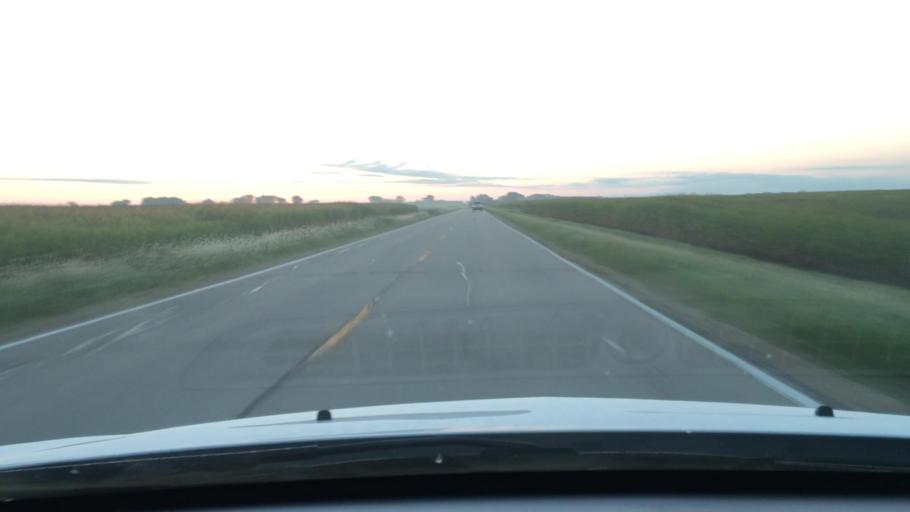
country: US
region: Illinois
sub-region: Ogle County
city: Rochelle
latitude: 41.8469
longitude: -89.0661
